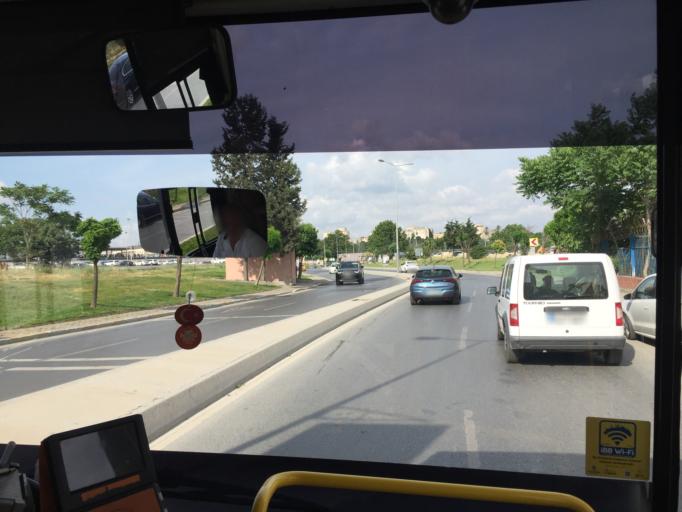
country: TR
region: Istanbul
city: Zeytinburnu
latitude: 40.9907
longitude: 28.9153
